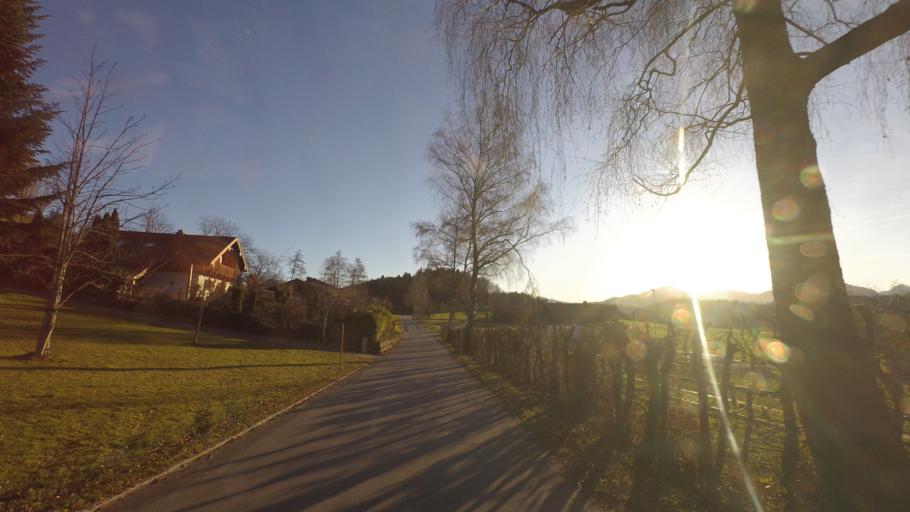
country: DE
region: Bavaria
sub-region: Upper Bavaria
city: Vachendorf
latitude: 47.8278
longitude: 12.6148
